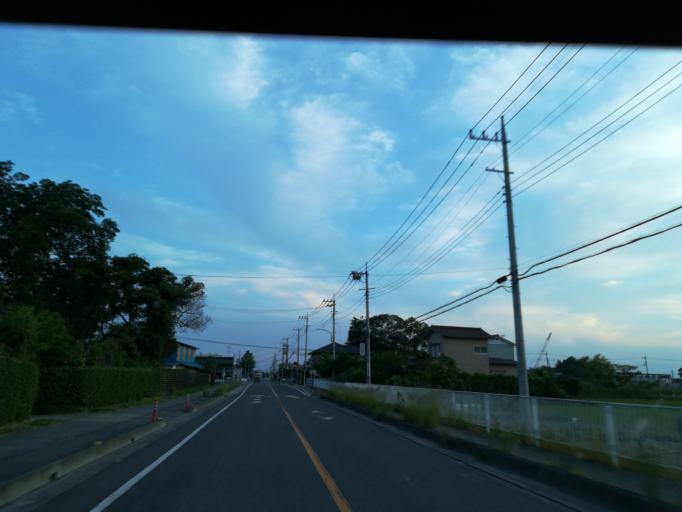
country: JP
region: Saitama
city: Kazo
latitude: 36.1475
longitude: 139.6164
